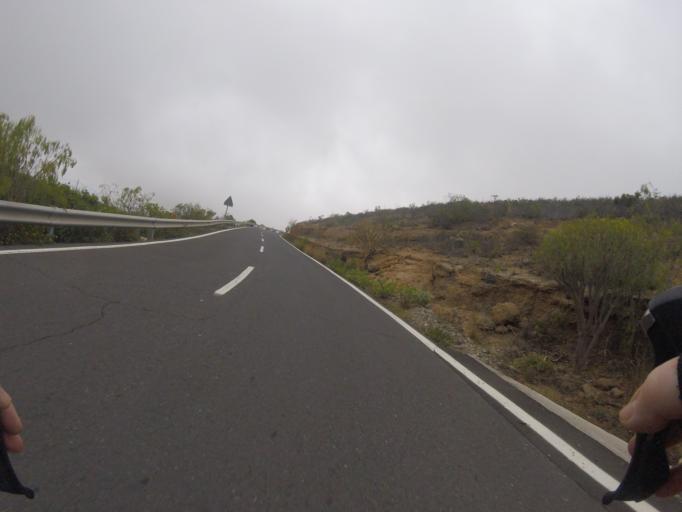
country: ES
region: Canary Islands
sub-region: Provincia de Santa Cruz de Tenerife
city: Lomo de Arico
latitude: 28.1968
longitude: -16.4728
